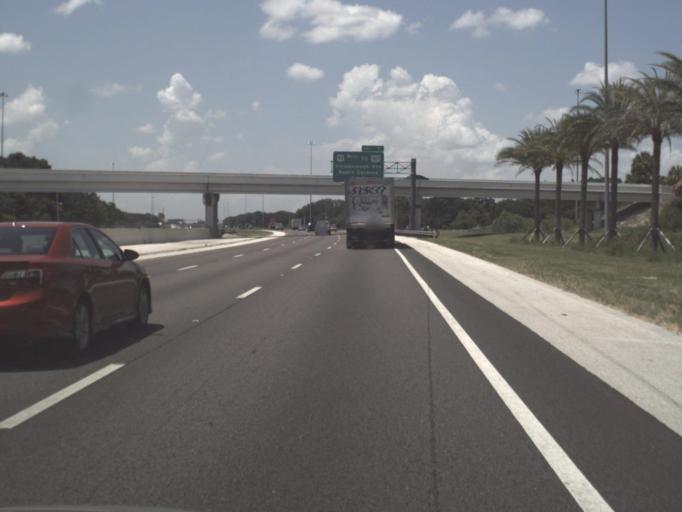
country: US
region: Florida
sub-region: Hillsborough County
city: Mango
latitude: 28.0020
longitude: -82.3291
